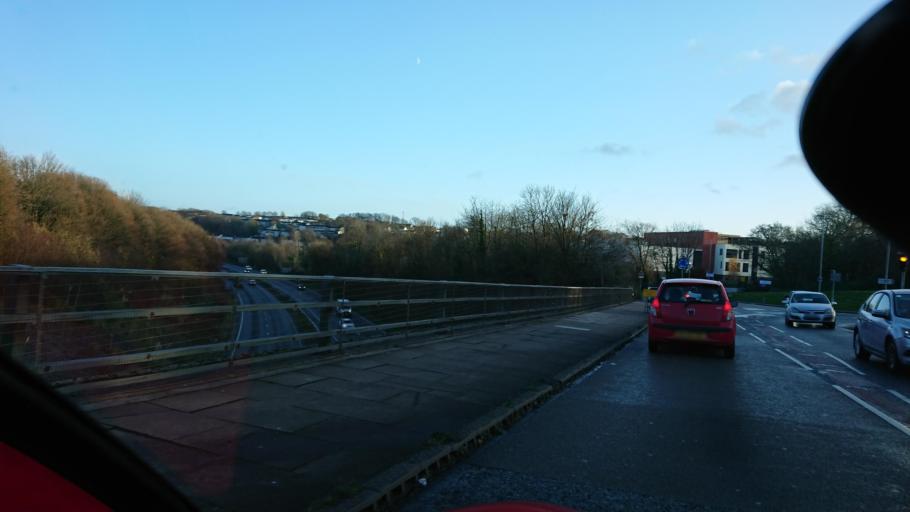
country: GB
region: England
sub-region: Plymouth
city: Plymouth
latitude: 50.4045
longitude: -4.1574
